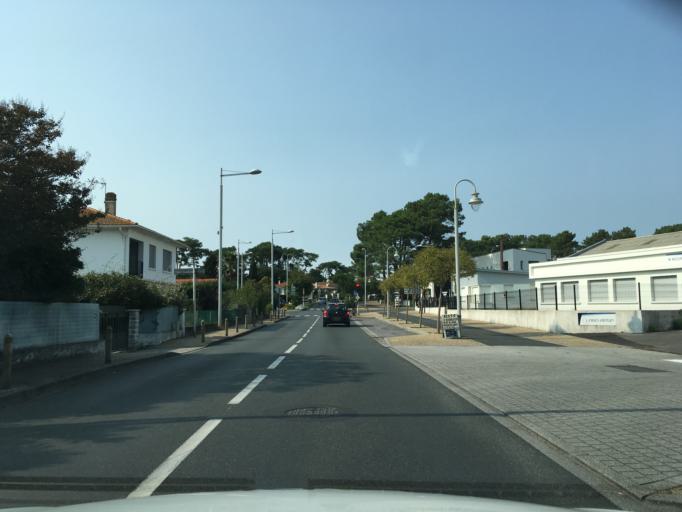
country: FR
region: Aquitaine
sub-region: Departement des Pyrenees-Atlantiques
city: Boucau
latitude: 43.5204
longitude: -1.5024
